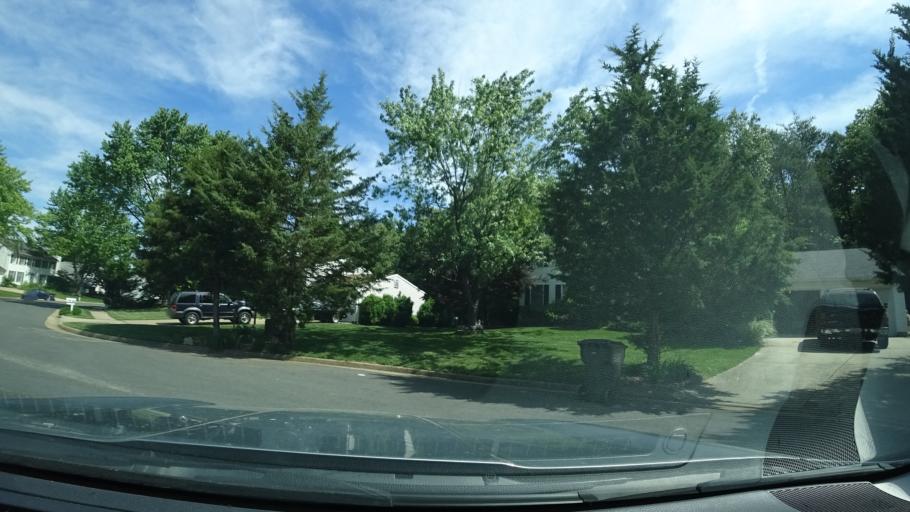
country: US
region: Virginia
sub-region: Loudoun County
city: Oak Grove
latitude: 38.9859
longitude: -77.4047
